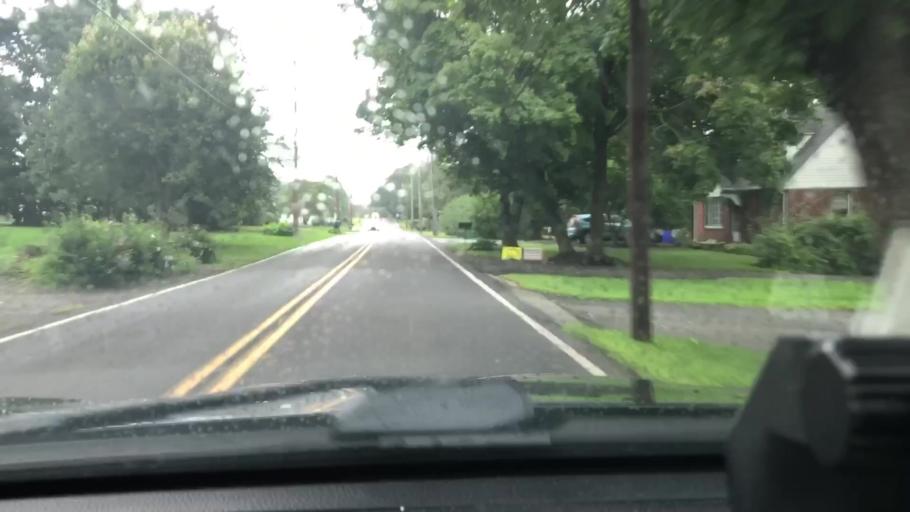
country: US
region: Pennsylvania
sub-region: Bucks County
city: Spinnerstown
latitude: 40.4356
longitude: -75.4324
